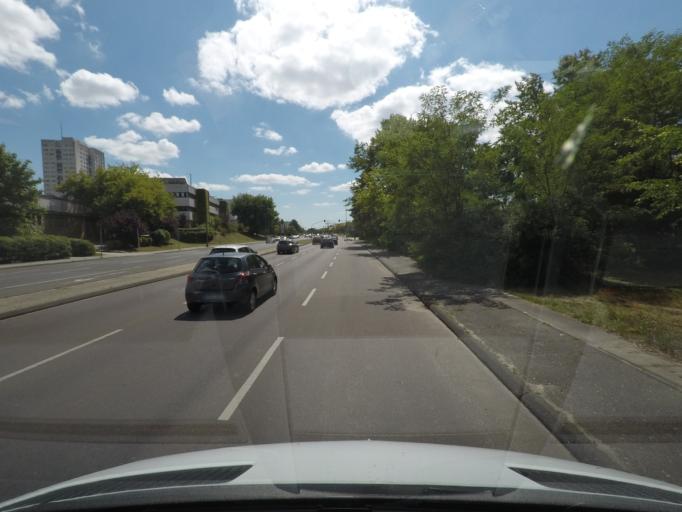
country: DE
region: Berlin
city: Biesdorf
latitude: 52.5365
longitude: 13.5375
